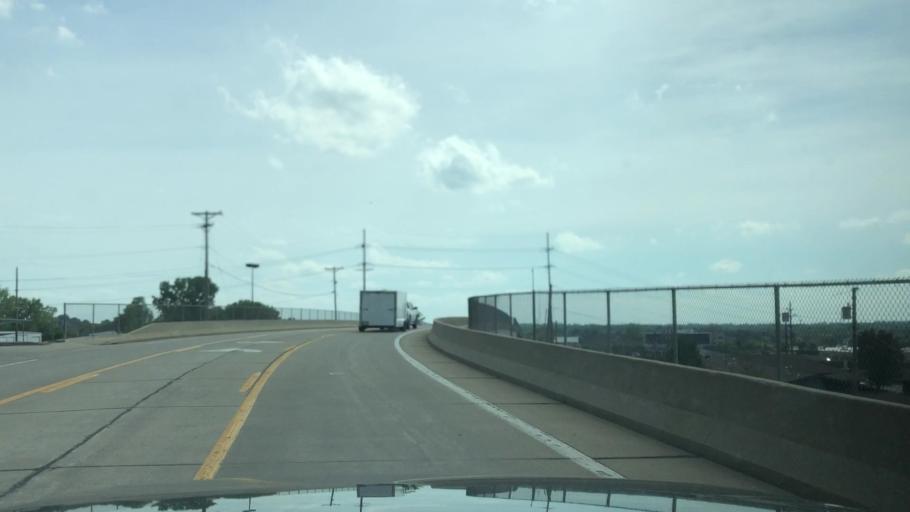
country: US
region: Missouri
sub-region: Saint Charles County
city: Saint Charles
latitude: 38.7829
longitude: -90.5177
